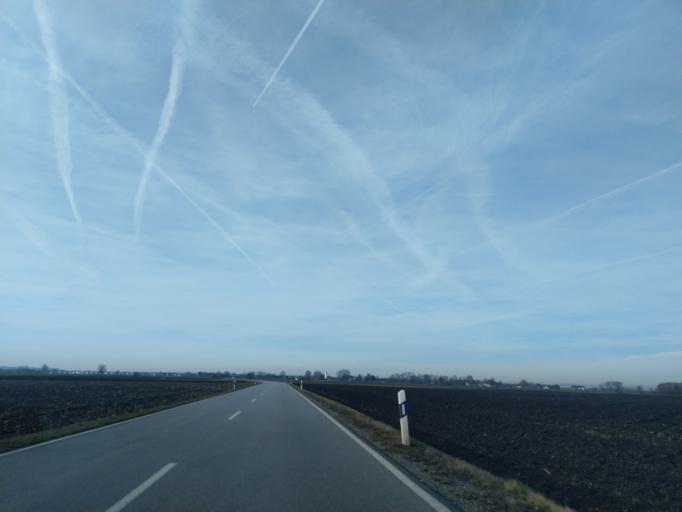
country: DE
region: Bavaria
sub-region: Lower Bavaria
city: Oberporing
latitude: 48.7220
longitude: 12.7900
